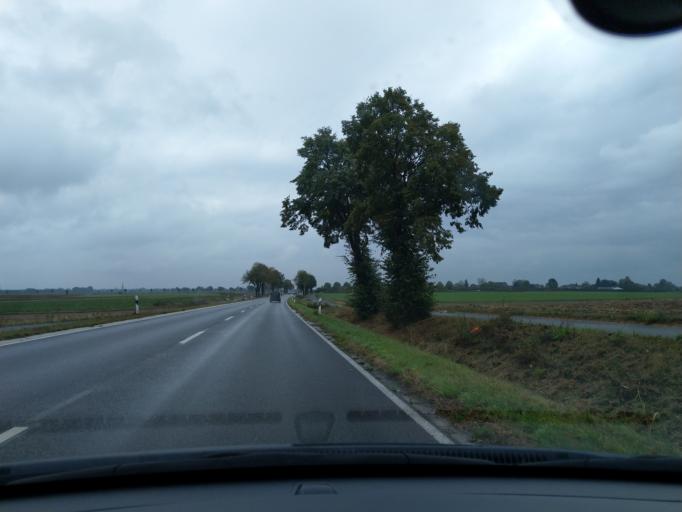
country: DE
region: North Rhine-Westphalia
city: Wegberg
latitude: 51.1132
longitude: 6.2944
